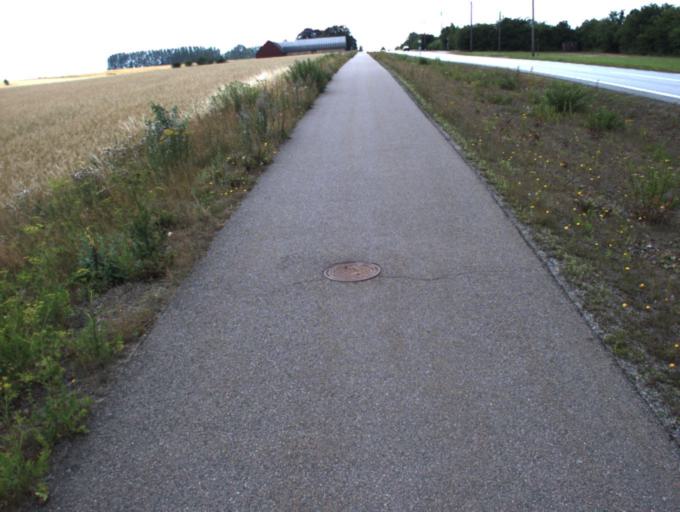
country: SE
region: Skane
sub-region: Helsingborg
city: Gantofta
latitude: 55.9970
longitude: 12.7739
